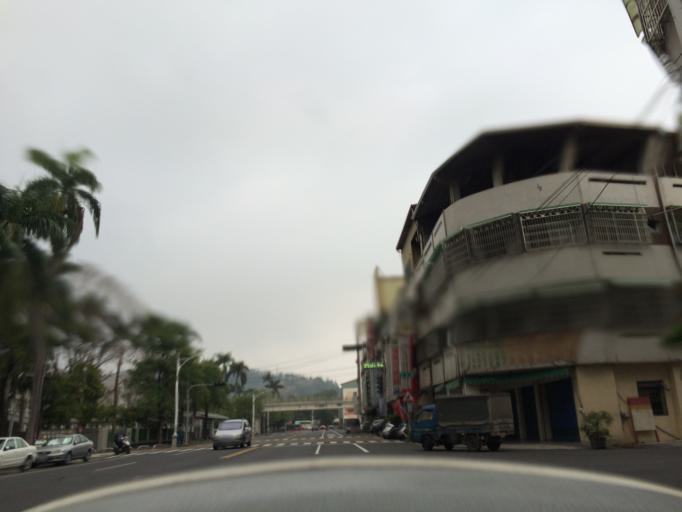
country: TW
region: Taiwan
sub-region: Taichung City
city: Taichung
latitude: 24.0589
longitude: 120.6978
